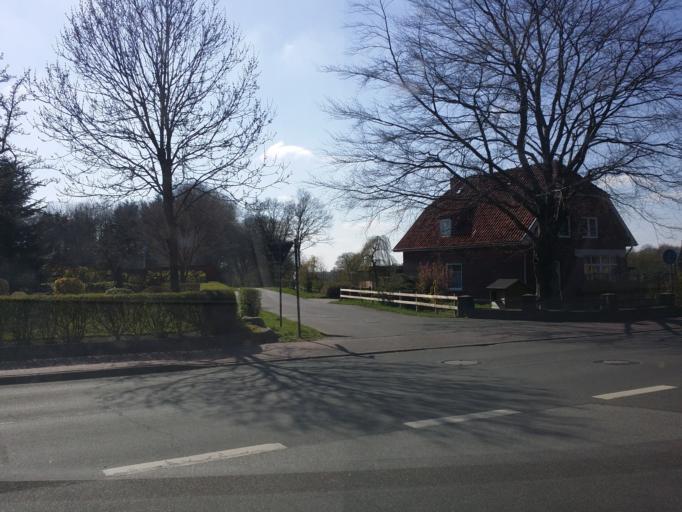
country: DE
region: Schleswig-Holstein
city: Wacken
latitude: 54.0246
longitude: 9.3689
